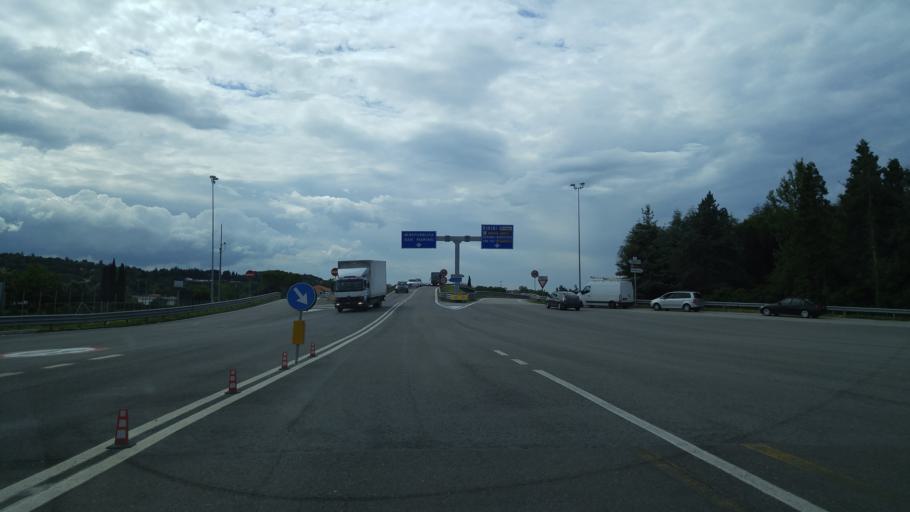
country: IT
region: Emilia-Romagna
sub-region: Provincia di Rimini
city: Rimini
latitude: 44.0359
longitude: 12.5659
